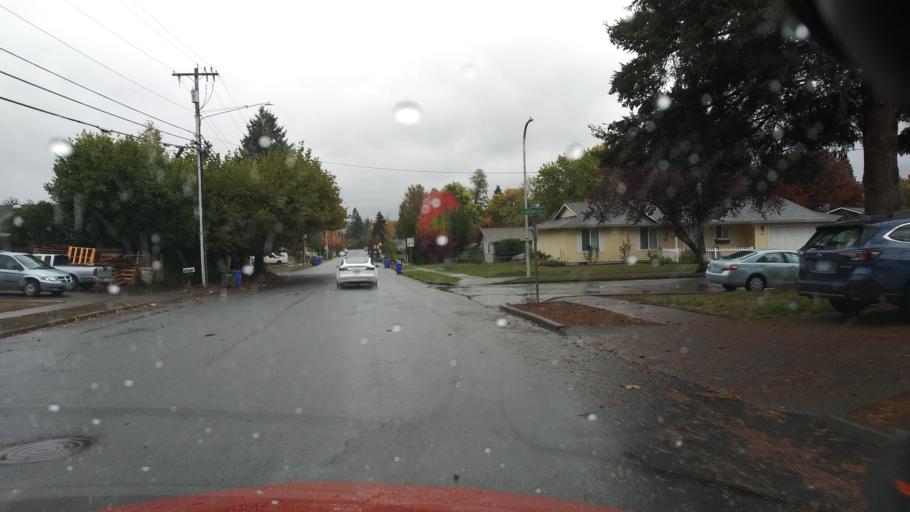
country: US
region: Oregon
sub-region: Washington County
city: Cornelius
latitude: 45.5174
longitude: -123.0668
